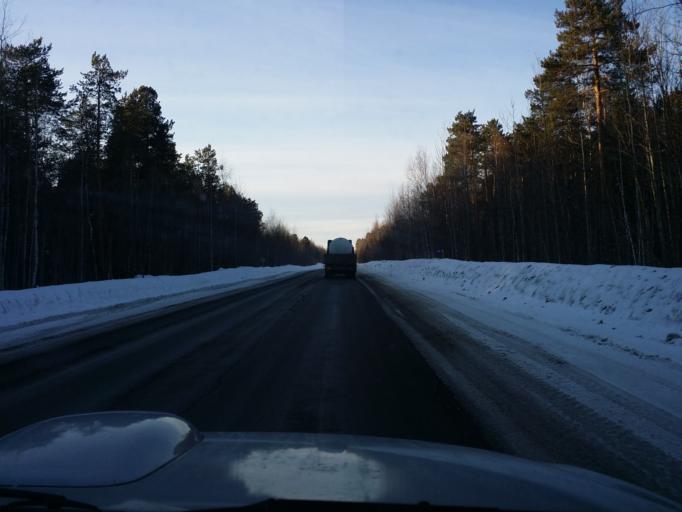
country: RU
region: Khanty-Mansiyskiy Avtonomnyy Okrug
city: Izluchinsk
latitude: 60.9458
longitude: 76.8542
